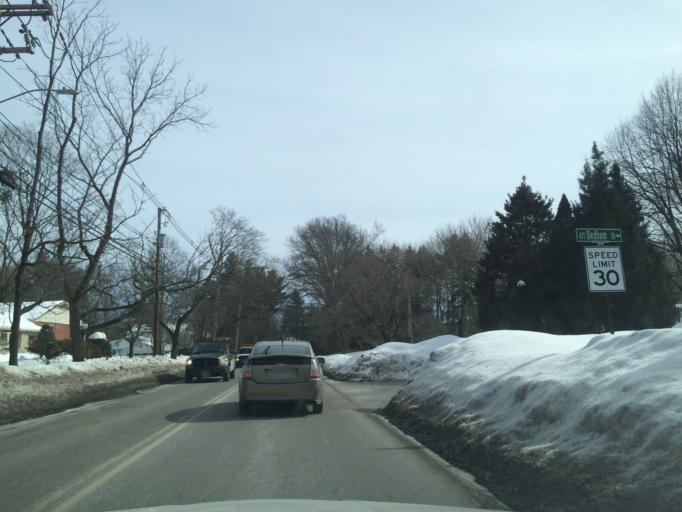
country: US
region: Massachusetts
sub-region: Middlesex County
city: Newton
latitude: 42.3077
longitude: -71.1970
